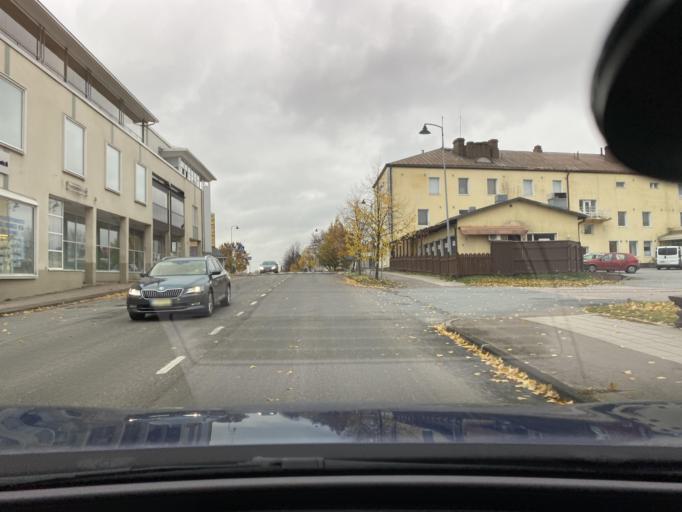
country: FI
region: Varsinais-Suomi
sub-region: Vakka-Suomi
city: Laitila
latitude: 60.8793
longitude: 21.6950
